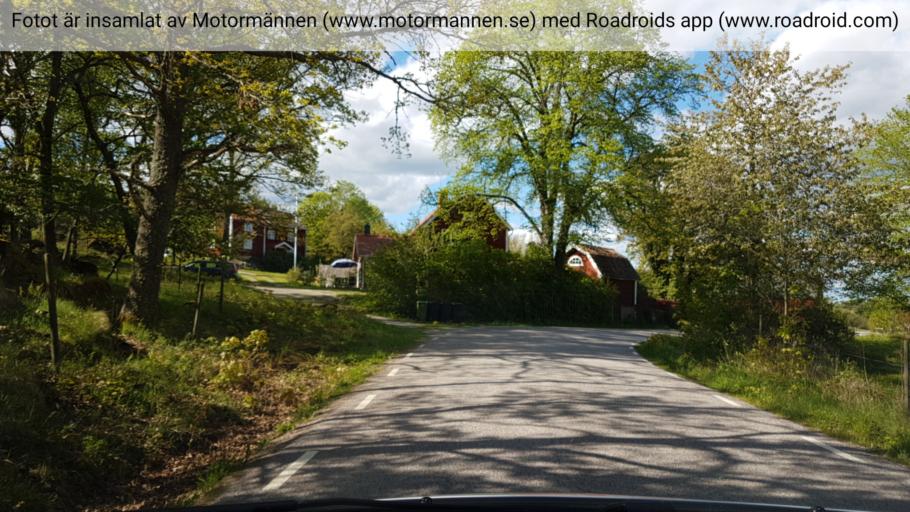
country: SE
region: Kalmar
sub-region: Vasterviks Kommun
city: Forserum
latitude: 57.9287
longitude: 16.4556
